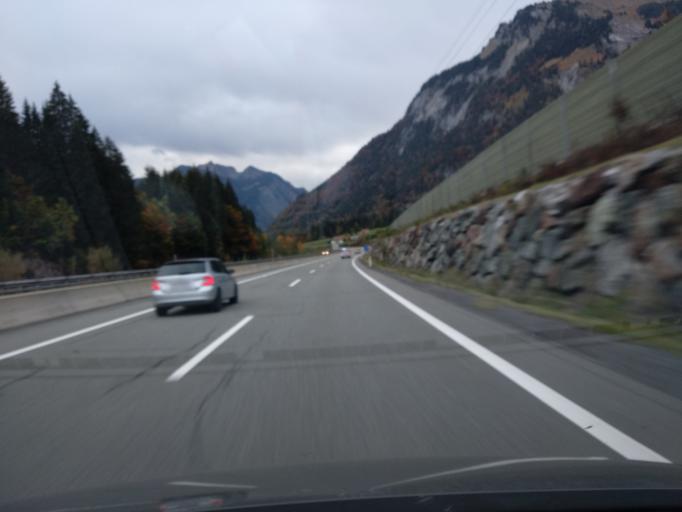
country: AT
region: Vorarlberg
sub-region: Politischer Bezirk Bludenz
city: Klosterle
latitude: 47.1277
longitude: 10.0396
